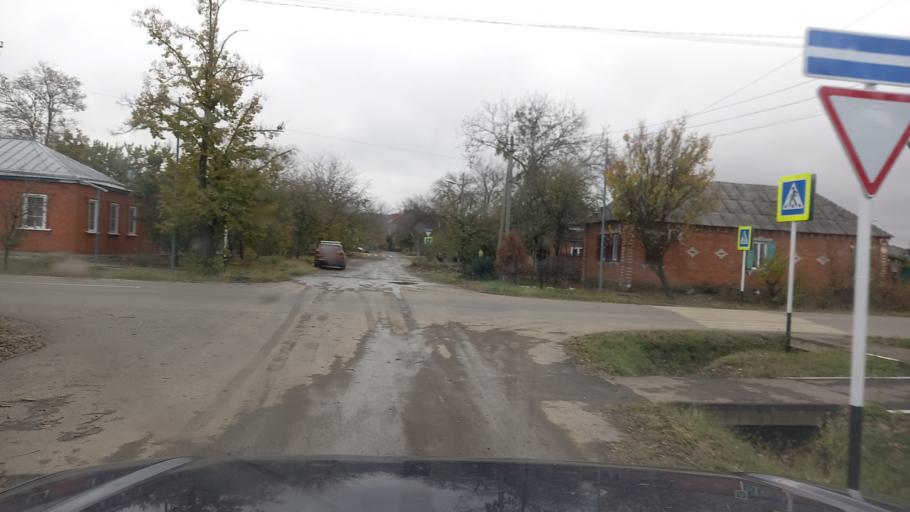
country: RU
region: Adygeya
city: Maykop
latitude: 44.6031
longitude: 40.0855
